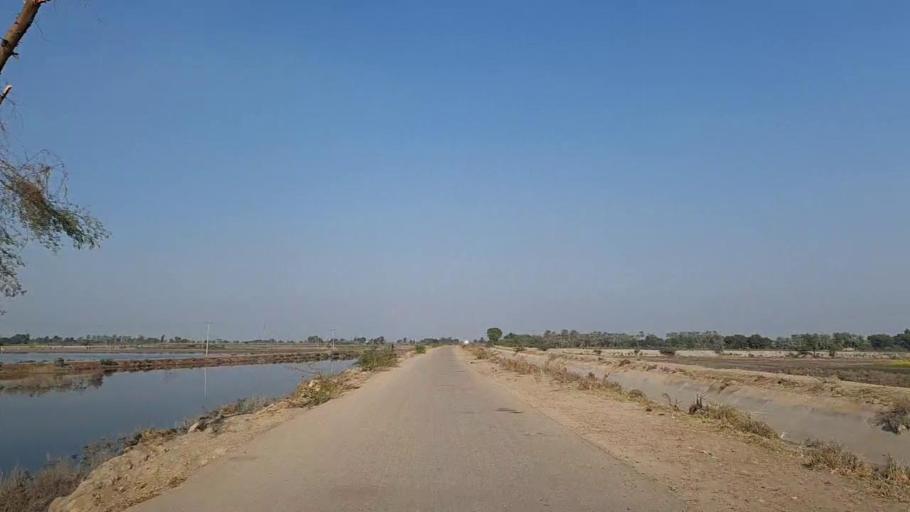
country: PK
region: Sindh
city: Daur
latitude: 26.4300
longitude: 68.2657
